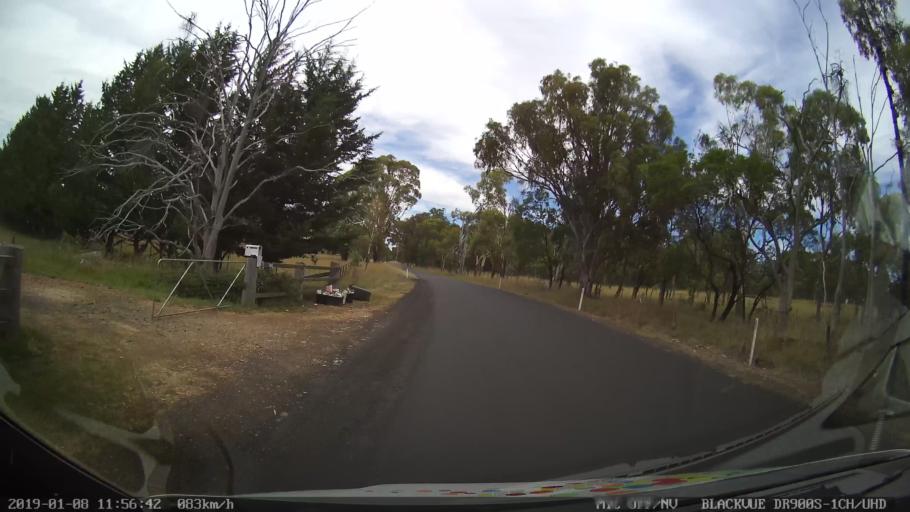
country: AU
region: New South Wales
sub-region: Armidale Dumaresq
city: Armidale
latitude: -30.4428
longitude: 151.5647
